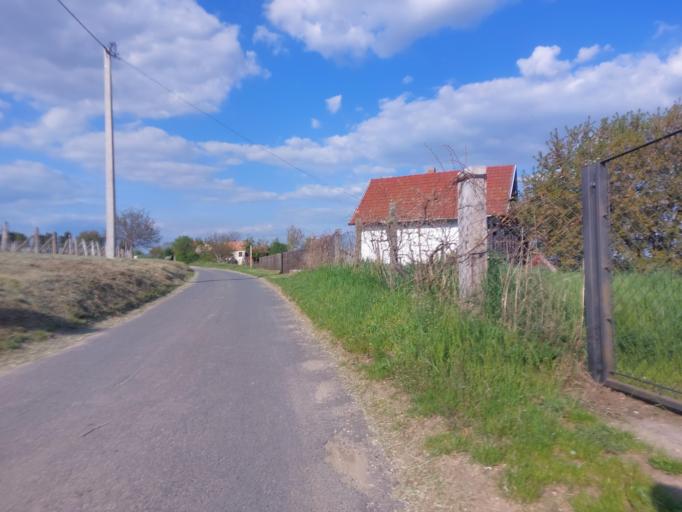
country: HU
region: Veszprem
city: Devecser
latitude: 47.1354
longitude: 17.3811
